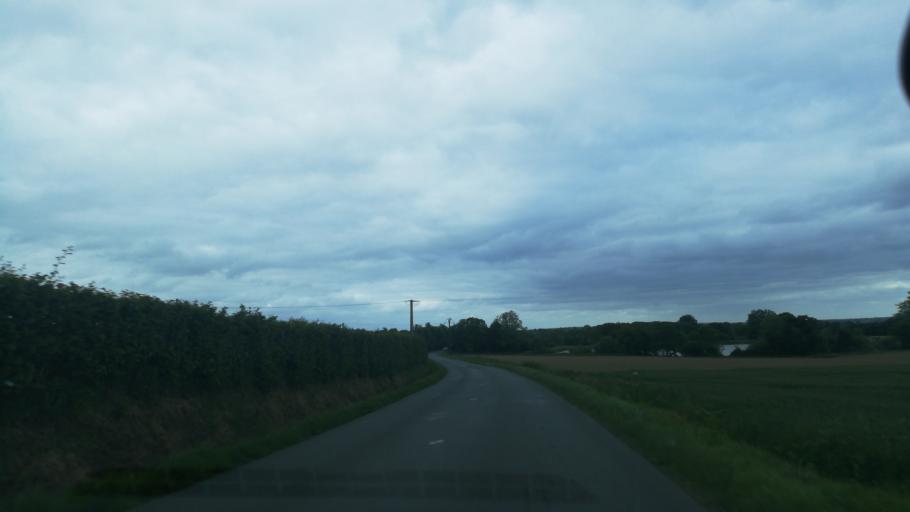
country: FR
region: Poitou-Charentes
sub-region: Departement des Deux-Sevres
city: La Chapelle-Saint-Laurent
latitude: 46.7647
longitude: -0.5147
